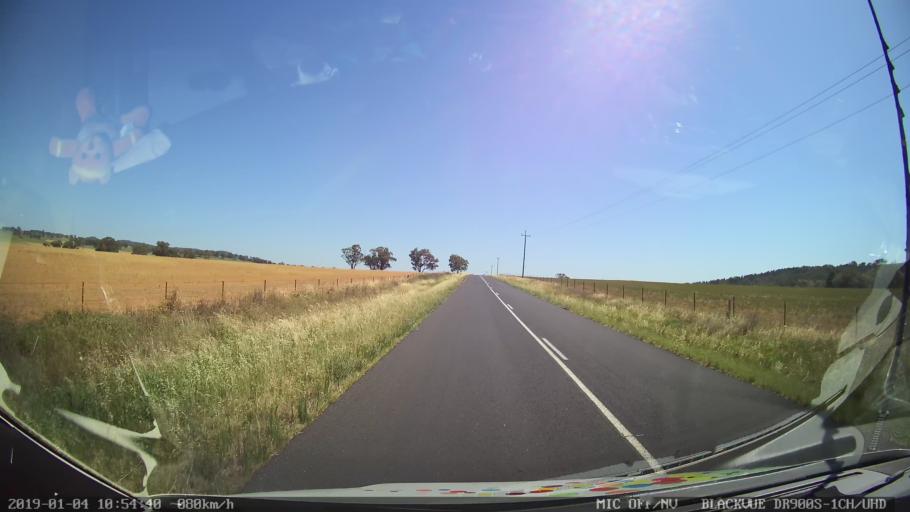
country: AU
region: New South Wales
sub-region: Cabonne
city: Molong
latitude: -33.2024
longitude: 148.6905
